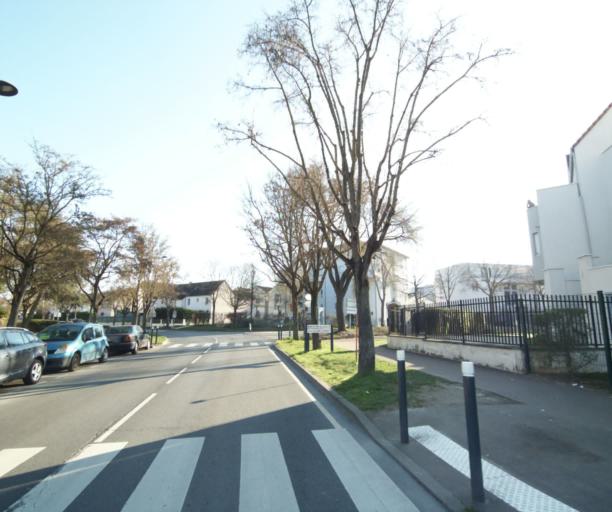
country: FR
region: Ile-de-France
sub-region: Departement du Val-d'Oise
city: Vaureal
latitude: 49.0470
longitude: 2.0364
